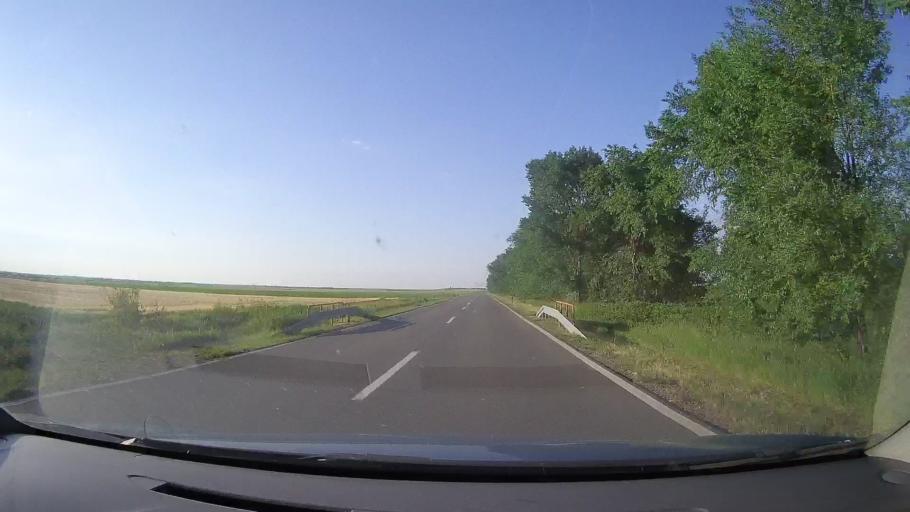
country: RS
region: Autonomna Pokrajina Vojvodina
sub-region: Juznobanatski Okrug
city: Vrsac
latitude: 45.1786
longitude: 21.2953
